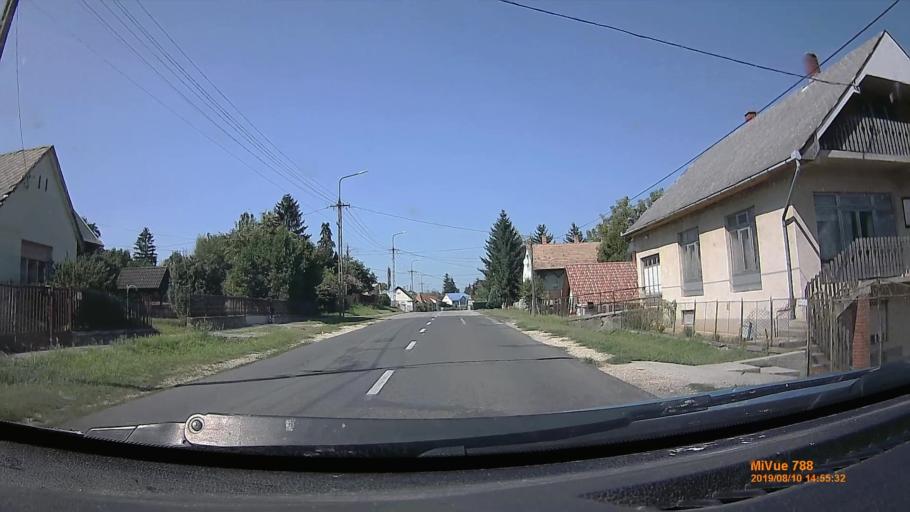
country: HU
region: Somogy
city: Lengyeltoti
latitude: 46.6619
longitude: 17.6357
